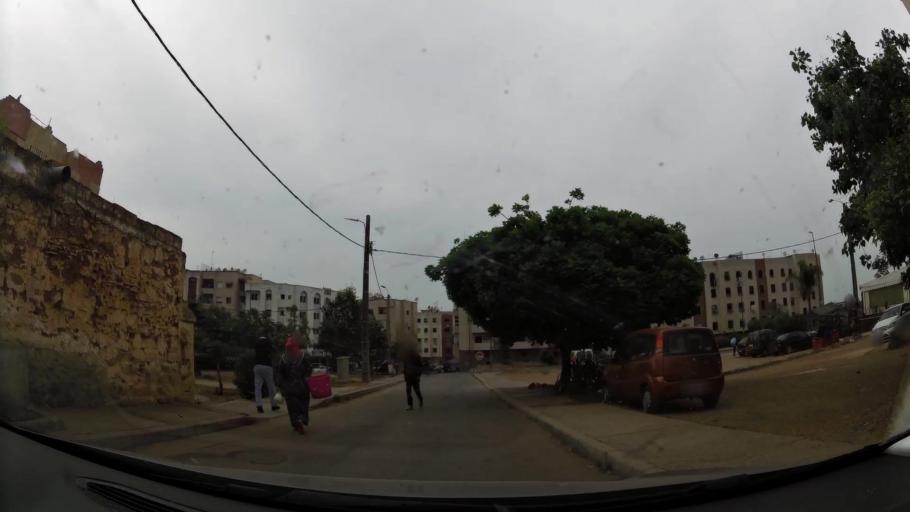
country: MA
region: Rabat-Sale-Zemmour-Zaer
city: Sale
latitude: 34.0334
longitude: -6.8011
